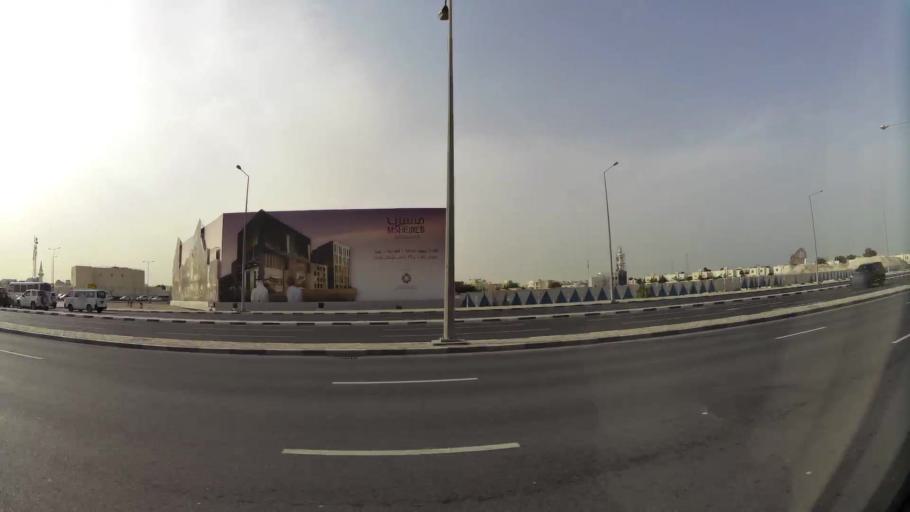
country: QA
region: Baladiyat ad Dawhah
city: Doha
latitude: 25.3201
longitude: 51.5134
